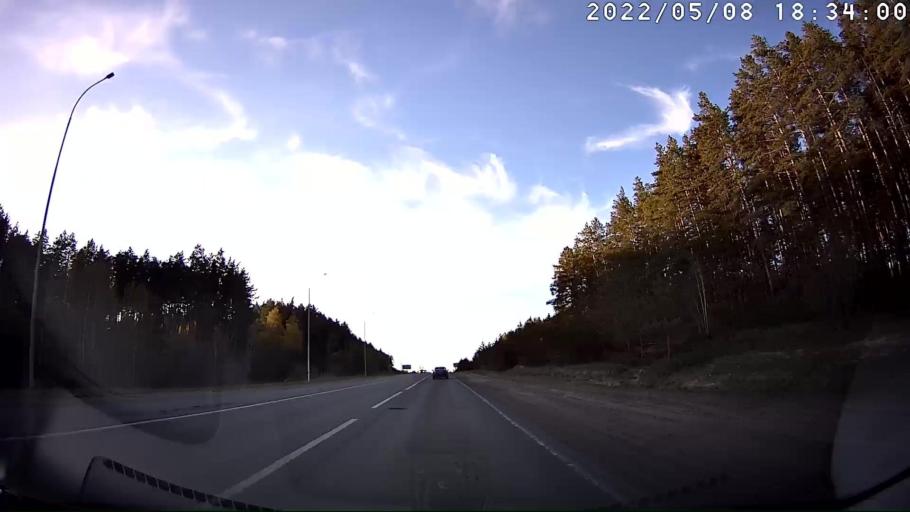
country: RU
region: Mariy-El
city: Volzhsk
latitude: 55.8958
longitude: 48.3565
